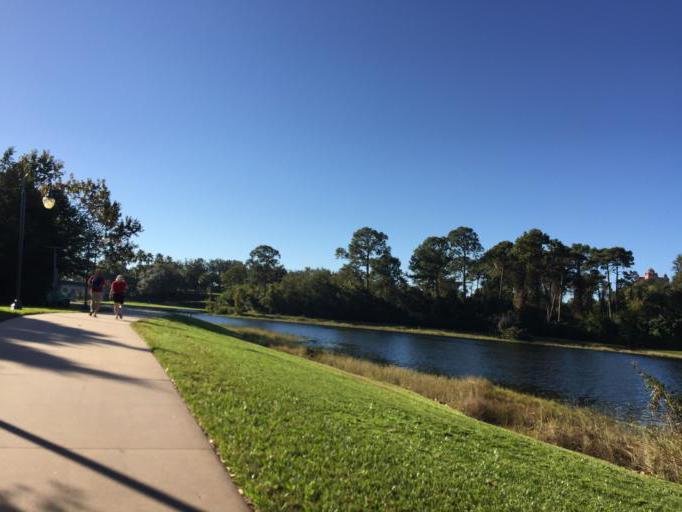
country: US
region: Florida
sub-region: Osceola County
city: Celebration
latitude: 28.3642
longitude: -81.5564
